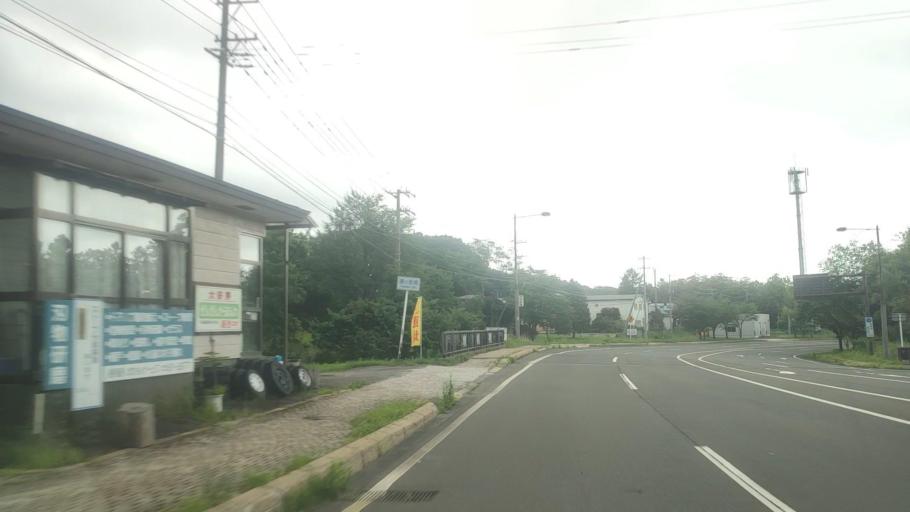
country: JP
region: Hokkaido
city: Shiraoi
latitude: 42.4714
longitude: 141.1584
